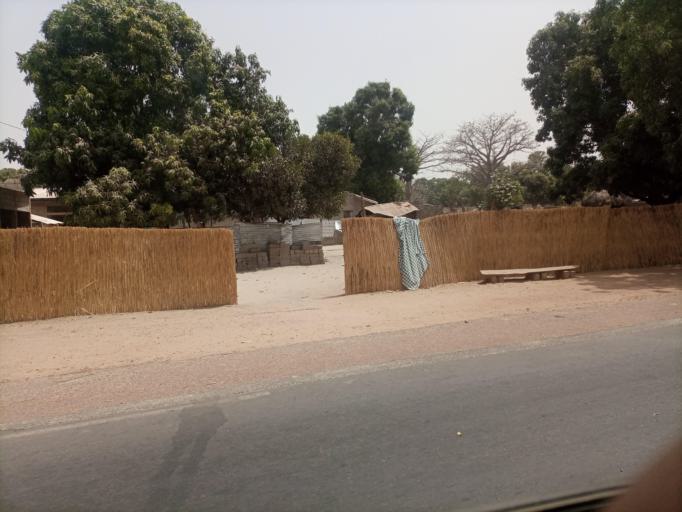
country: SN
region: Fatick
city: Sokone
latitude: 13.7413
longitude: -16.4287
